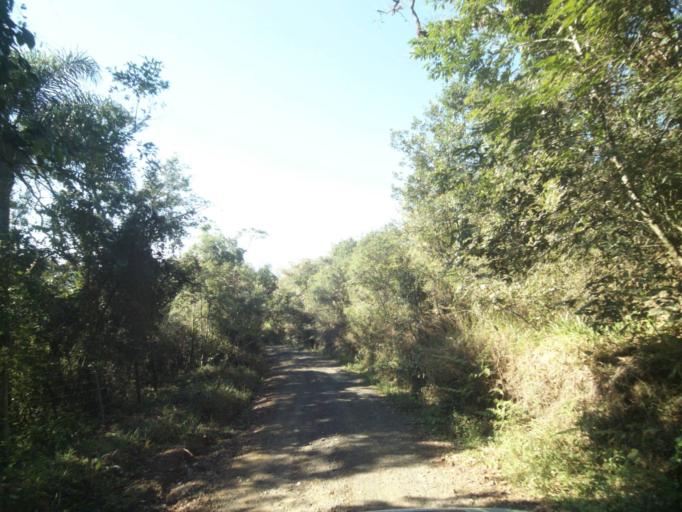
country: BR
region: Parana
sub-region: Tibagi
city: Tibagi
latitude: -24.5465
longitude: -50.4687
